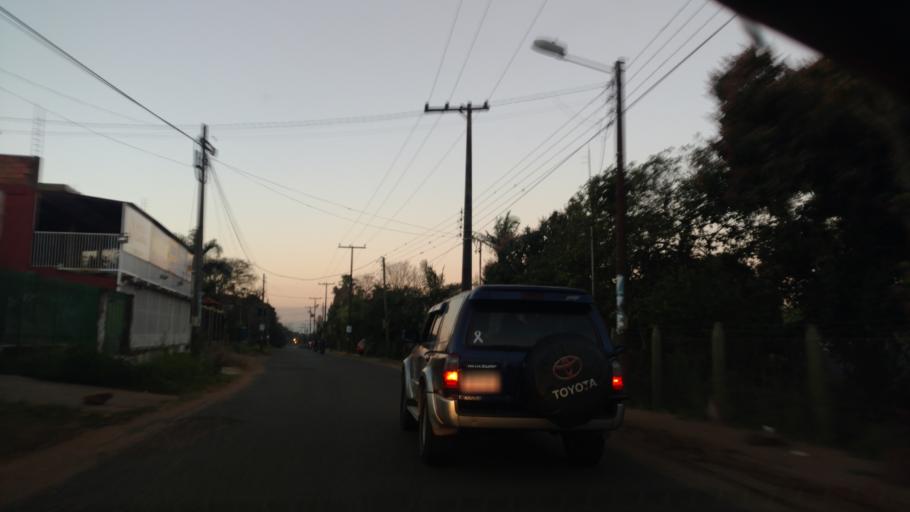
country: PY
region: Central
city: Guarambare
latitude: -25.4746
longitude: -57.4125
